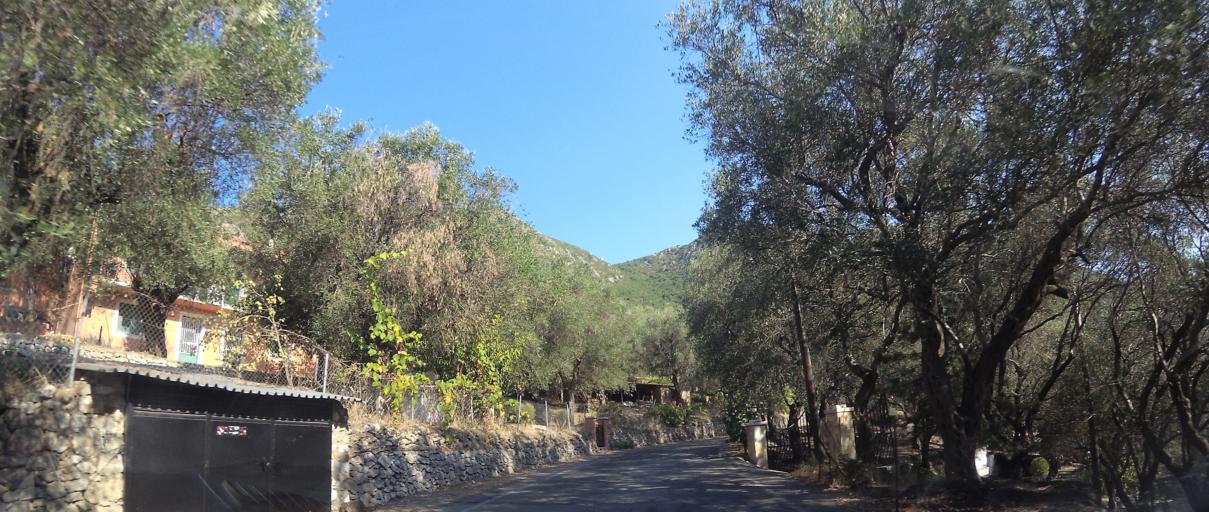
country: GR
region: Ionian Islands
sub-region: Nomos Kerkyras
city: Kontokali
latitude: 39.7204
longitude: 19.8464
